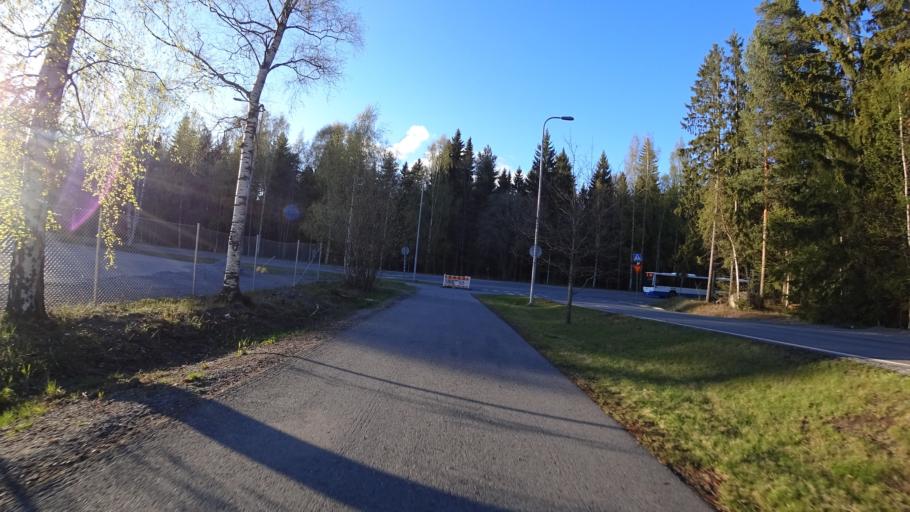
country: FI
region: Pirkanmaa
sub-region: Tampere
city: Pirkkala
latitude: 61.5041
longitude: 23.6105
